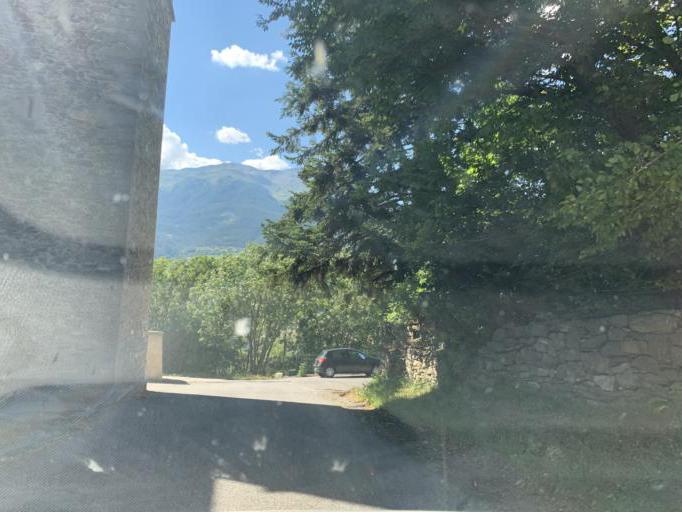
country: FR
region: Provence-Alpes-Cote d'Azur
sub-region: Departement des Hautes-Alpes
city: Embrun
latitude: 44.5869
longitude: 6.5343
